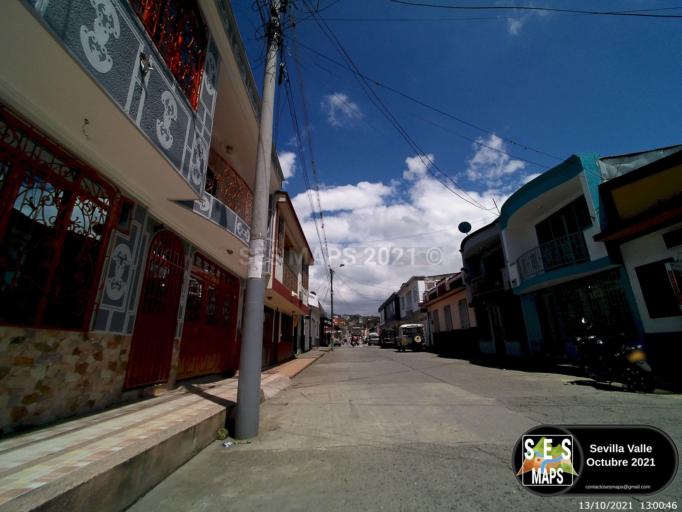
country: CO
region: Valle del Cauca
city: Sevilla
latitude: 4.2664
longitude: -75.9337
